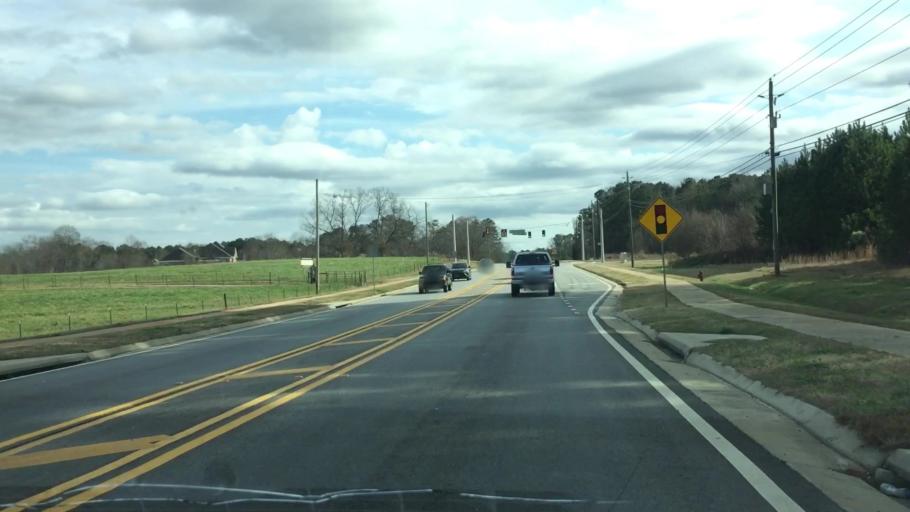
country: US
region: Georgia
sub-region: Henry County
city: McDonough
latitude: 33.4350
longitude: -84.1157
